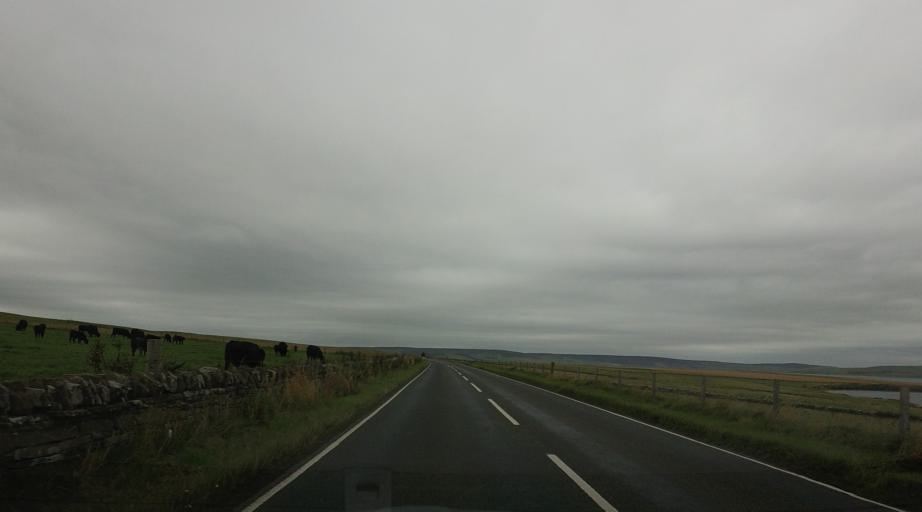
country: GB
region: Scotland
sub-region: Orkney Islands
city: Orkney
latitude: 59.0018
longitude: -2.9984
